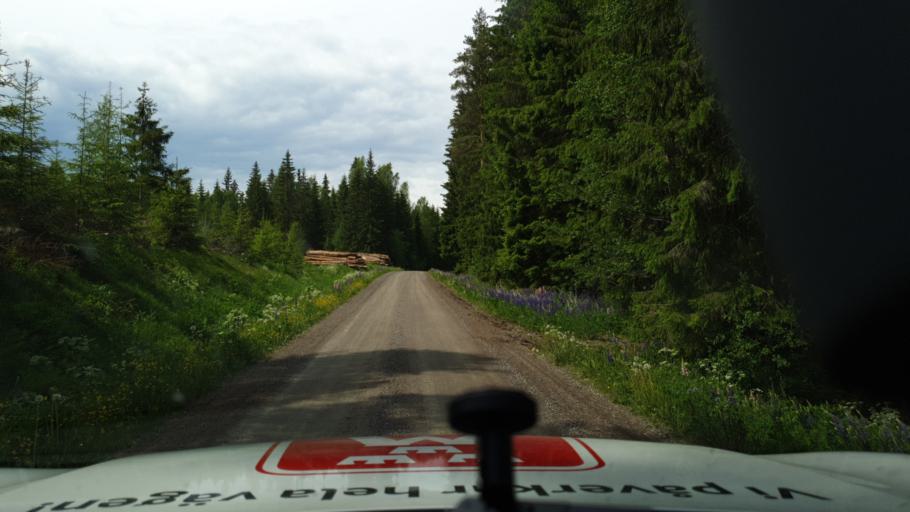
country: SE
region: Vaermland
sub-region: Torsby Kommun
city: Torsby
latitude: 59.9791
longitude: 12.8436
